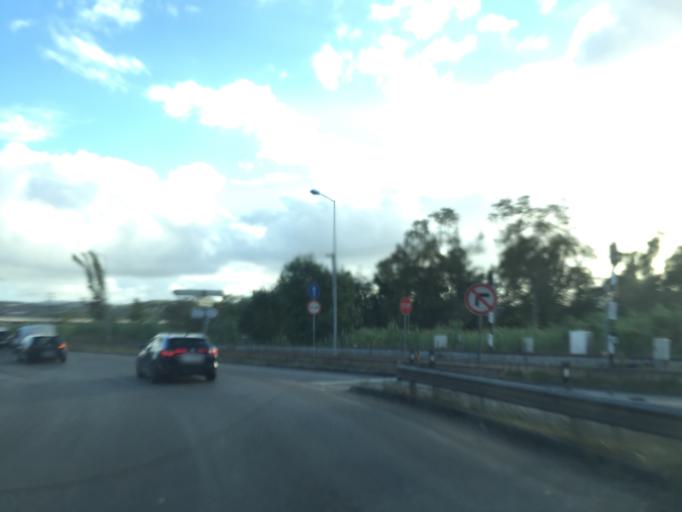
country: PT
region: Coimbra
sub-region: Coimbra
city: Coimbra
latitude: 40.2192
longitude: -8.4391
